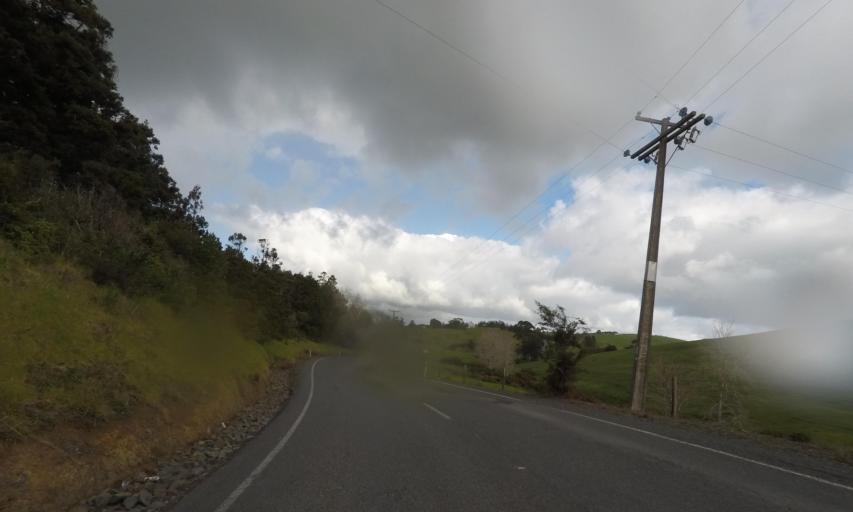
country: NZ
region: Auckland
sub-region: Auckland
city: Wellsford
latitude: -36.1711
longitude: 174.5825
